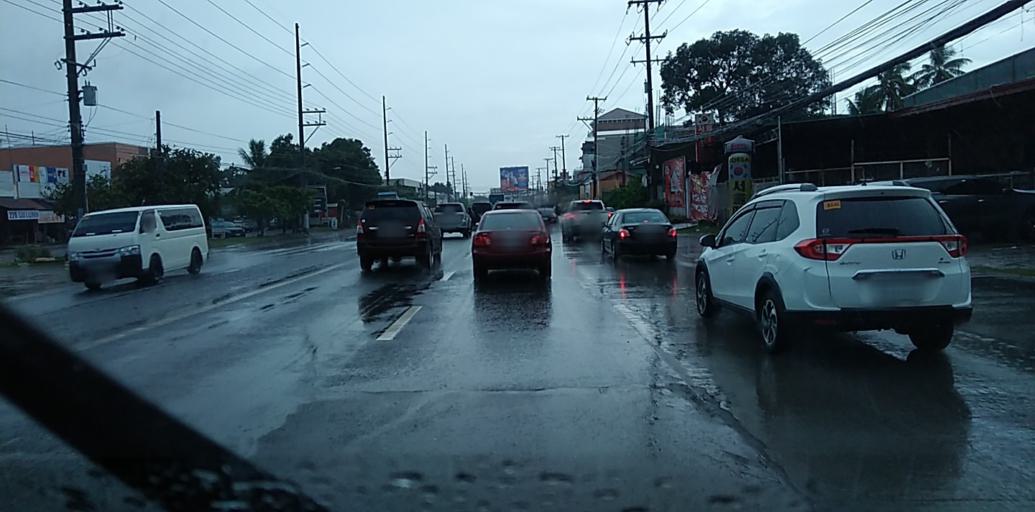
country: PH
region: Central Luzon
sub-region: Province of Pampanga
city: Magliman
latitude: 15.0515
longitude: 120.6637
